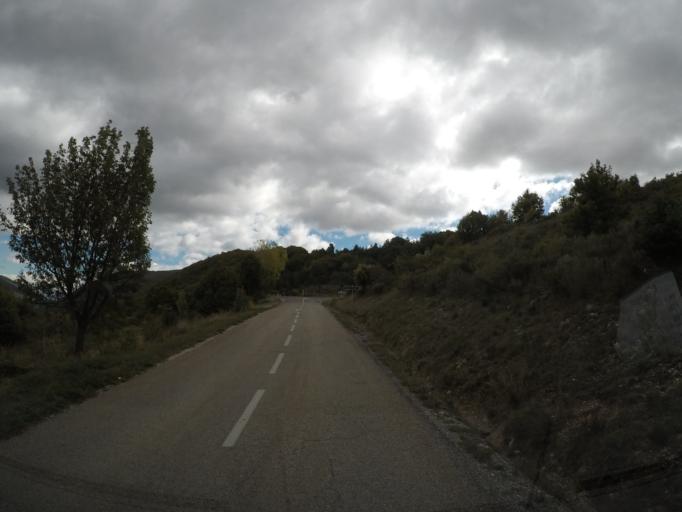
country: FR
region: Provence-Alpes-Cote d'Azur
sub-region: Departement du Vaucluse
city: Sault
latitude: 44.1828
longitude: 5.5091
